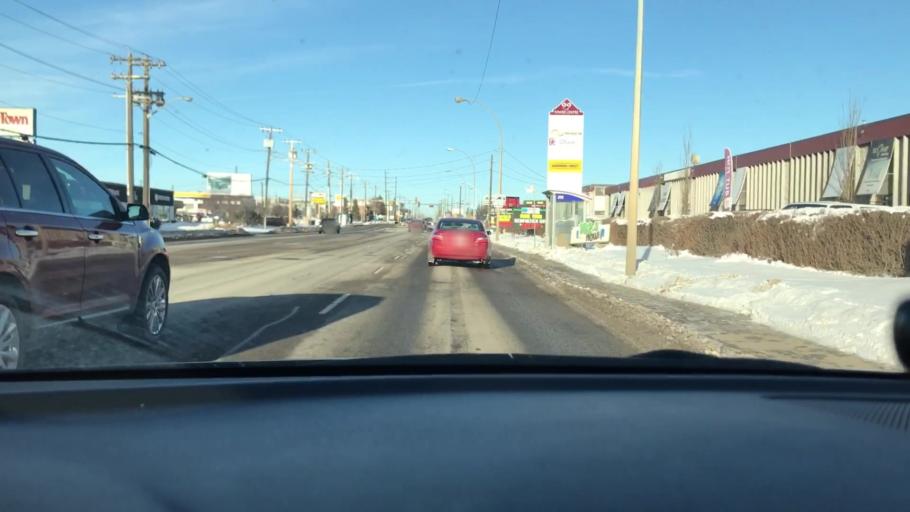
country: CA
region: Alberta
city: Edmonton
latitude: 53.4859
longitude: -113.4860
